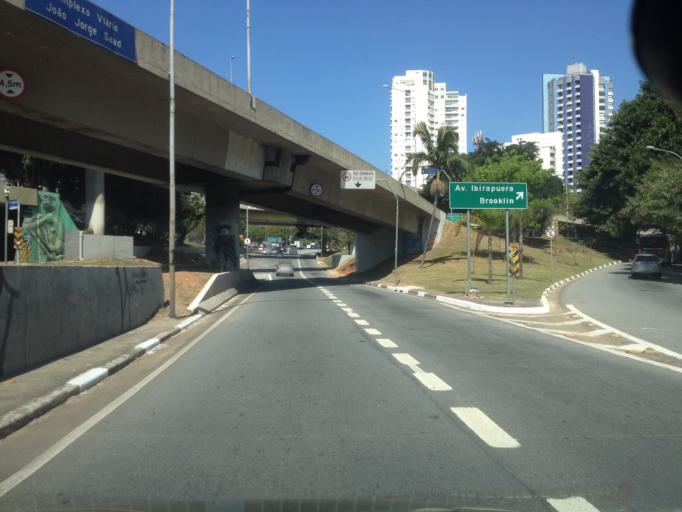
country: BR
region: Sao Paulo
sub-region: Sao Paulo
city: Sao Paulo
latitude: -23.5910
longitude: -46.6515
